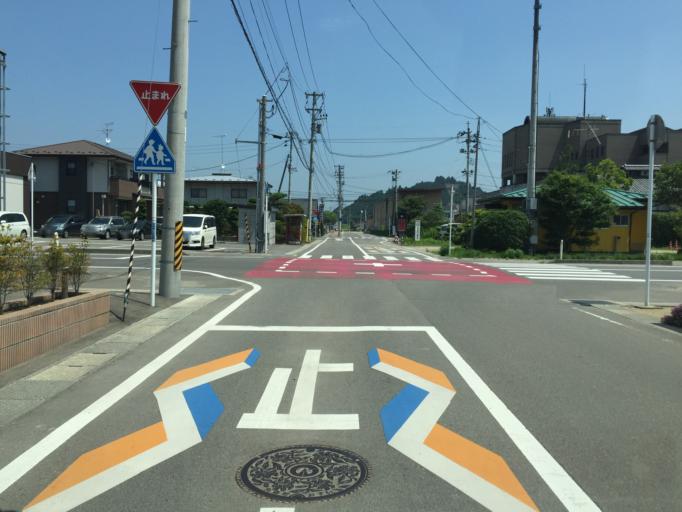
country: JP
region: Miyagi
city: Marumori
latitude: 37.9119
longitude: 140.7637
